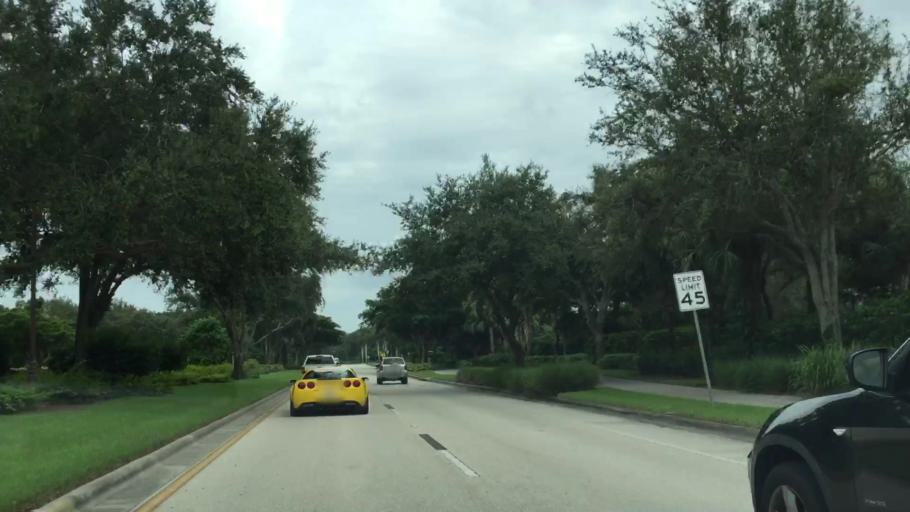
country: US
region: Florida
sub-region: Lee County
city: Estero
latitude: 26.3976
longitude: -81.7973
